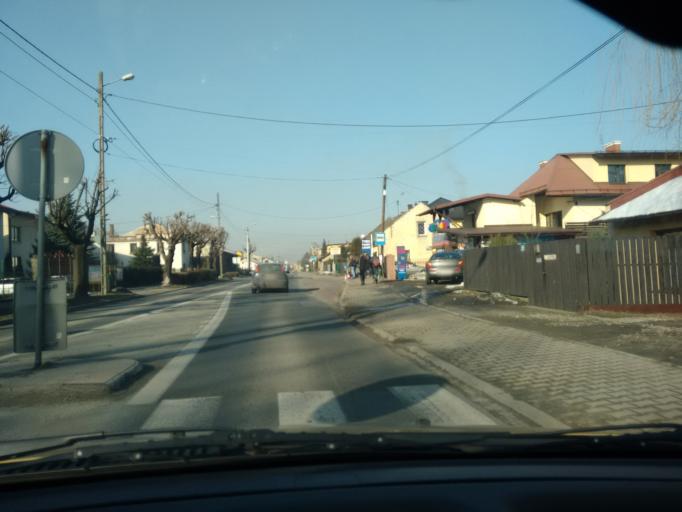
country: PL
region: Lesser Poland Voivodeship
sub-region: Powiat oswiecimski
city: Kety
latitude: 49.8768
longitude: 19.2240
